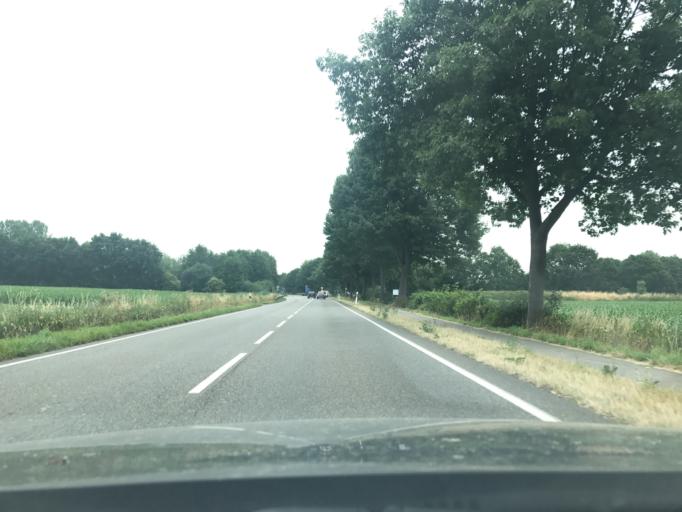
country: DE
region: North Rhine-Westphalia
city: Kempen
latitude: 51.4027
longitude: 6.4196
